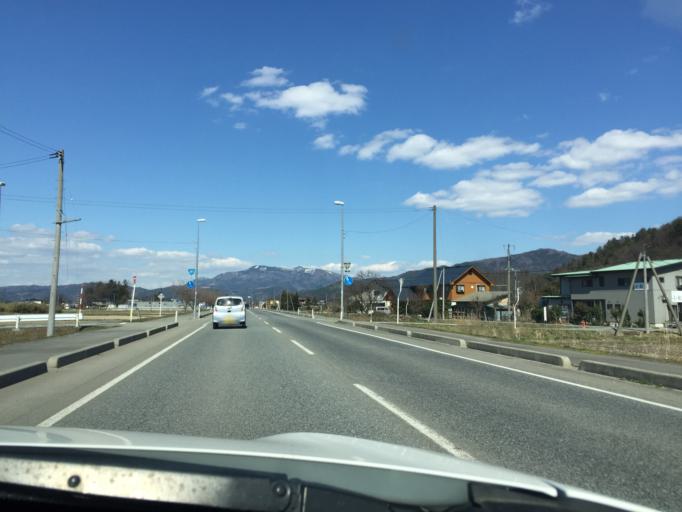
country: JP
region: Yamagata
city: Nagai
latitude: 38.1541
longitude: 140.0673
